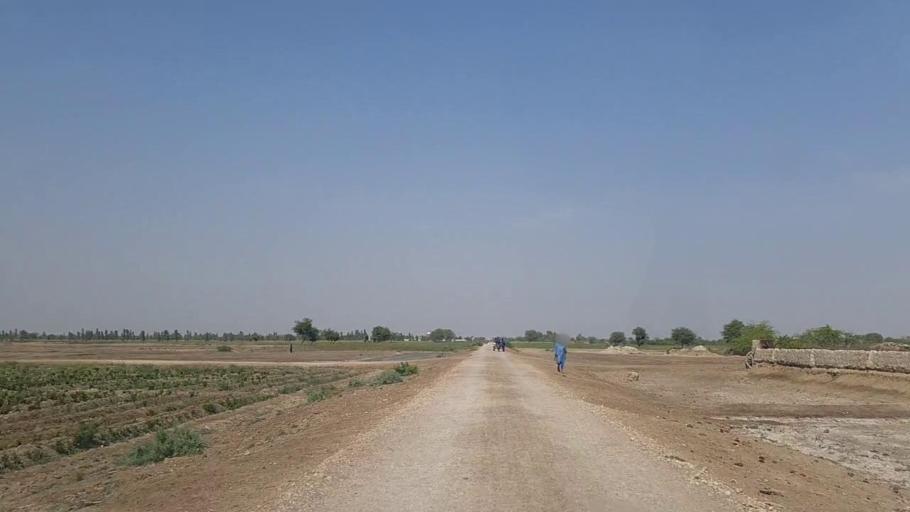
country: PK
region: Sindh
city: Samaro
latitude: 25.2593
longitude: 69.3947
